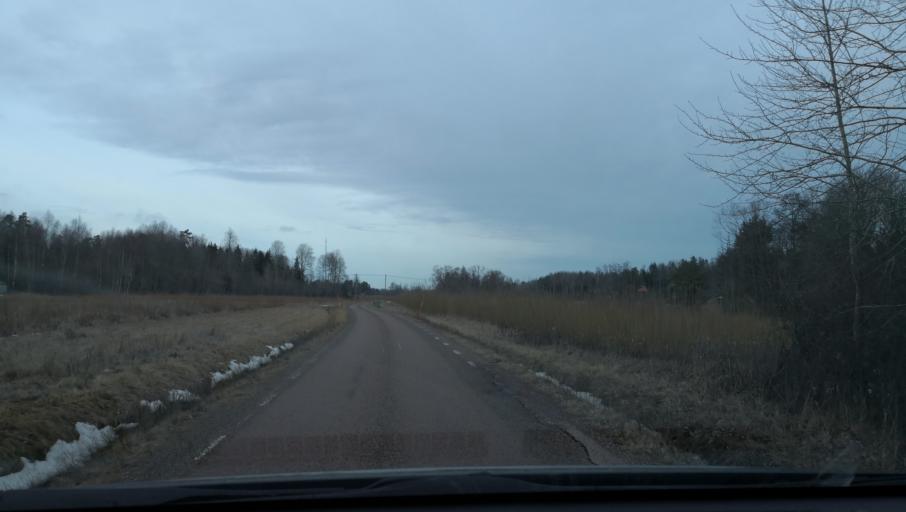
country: SE
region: Vaestmanland
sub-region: Vasteras
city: Skultuna
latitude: 59.6076
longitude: 16.4117
